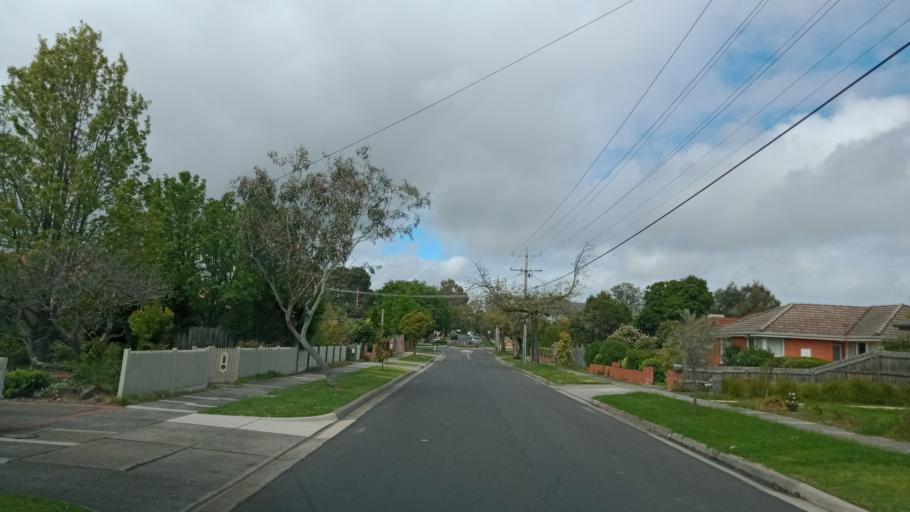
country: AU
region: Victoria
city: Burwood East
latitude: -37.8665
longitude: 145.1395
